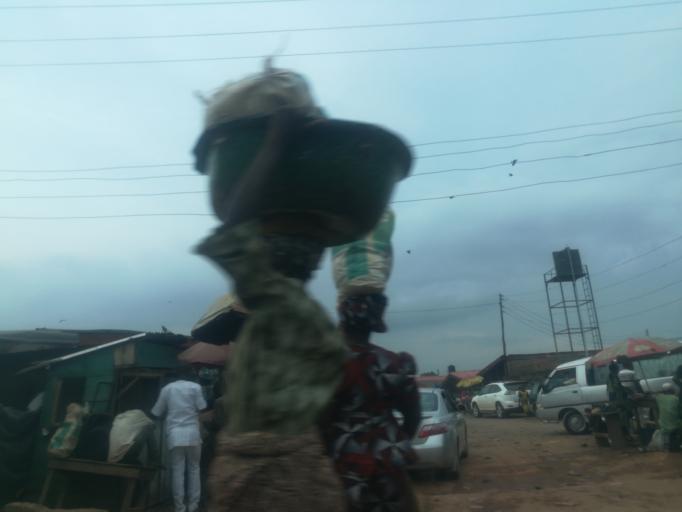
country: NG
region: Oyo
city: Ibadan
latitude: 7.4351
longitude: 3.9151
